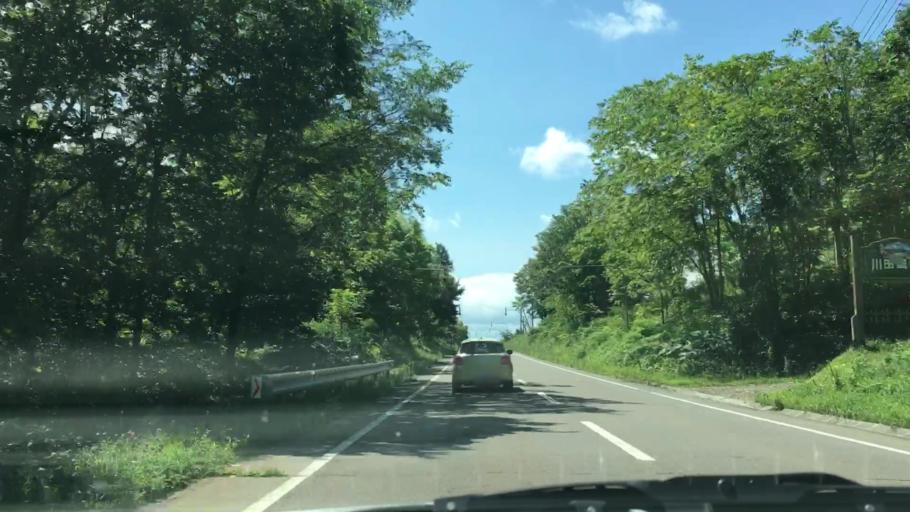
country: JP
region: Hokkaido
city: Otofuke
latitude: 43.2823
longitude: 143.6268
